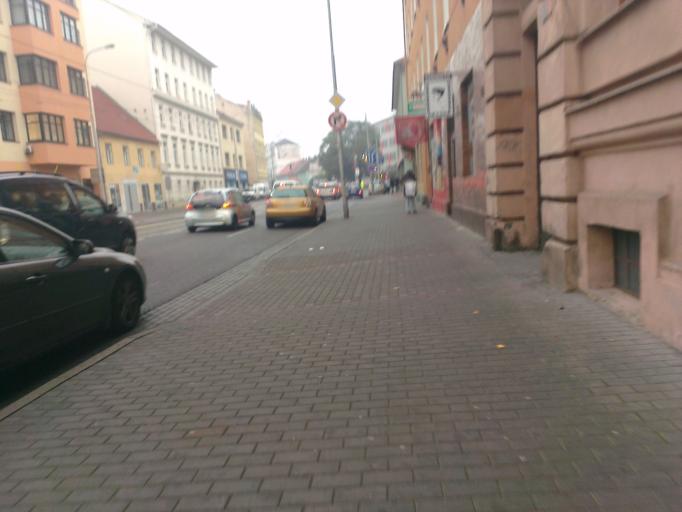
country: CZ
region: South Moravian
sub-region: Mesto Brno
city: Brno
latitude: 49.1914
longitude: 16.6203
